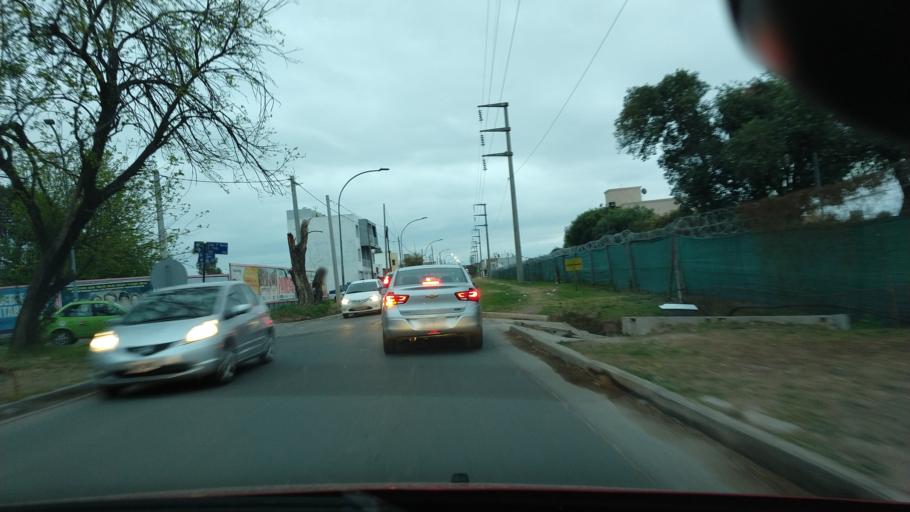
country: AR
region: Cordoba
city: La Calera
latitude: -31.3785
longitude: -64.2656
